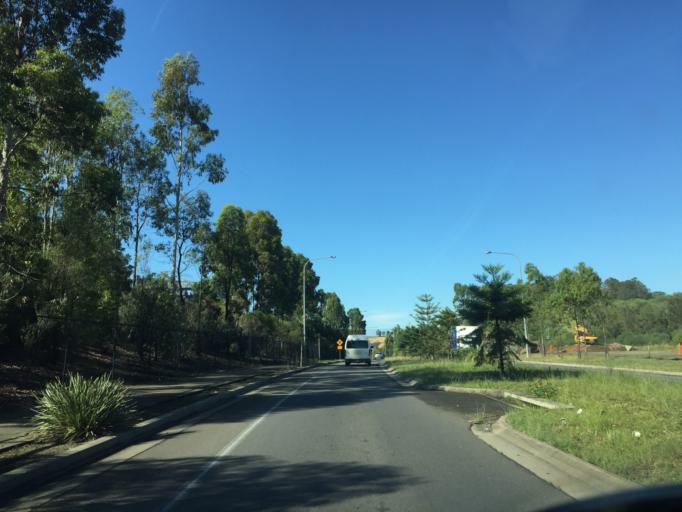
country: AU
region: New South Wales
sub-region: Holroyd
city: Girraween
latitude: -33.8167
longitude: 150.9205
